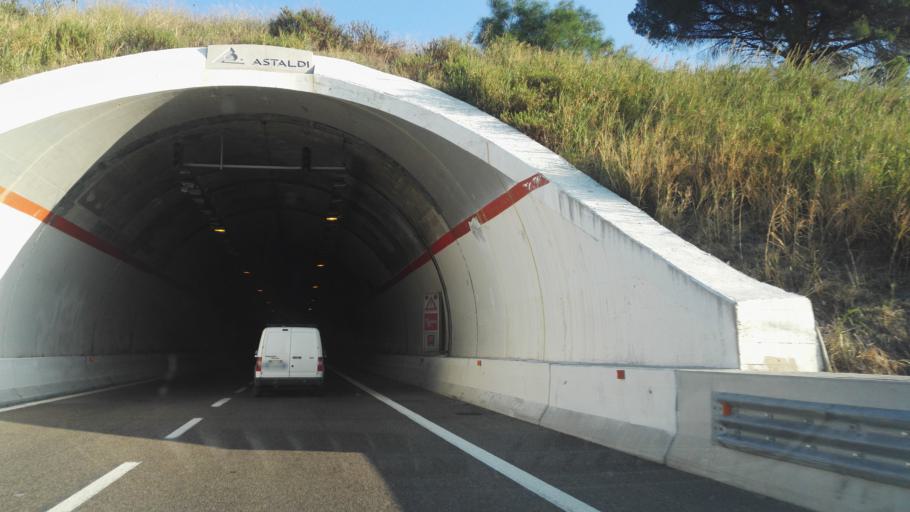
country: IT
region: Calabria
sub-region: Provincia di Catanzaro
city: Squillace Lido
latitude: 38.7846
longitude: 16.5513
